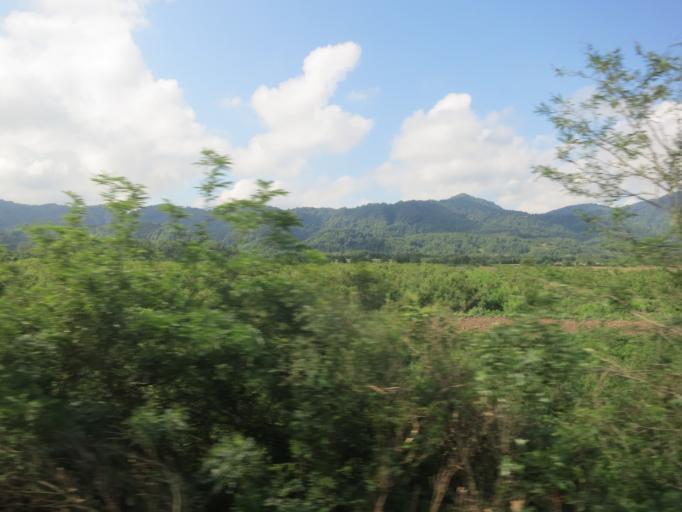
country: GE
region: Guria
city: Lanchkhuti
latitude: 42.0844
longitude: 42.0734
